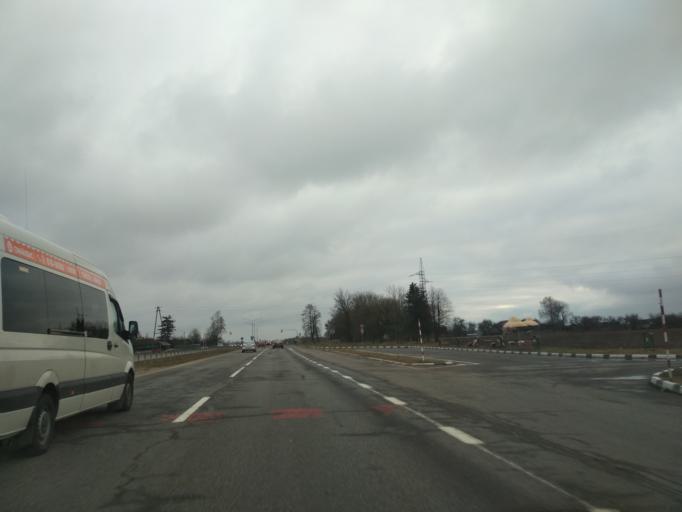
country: BY
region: Minsk
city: Dukora
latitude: 53.6712
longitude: 27.9343
